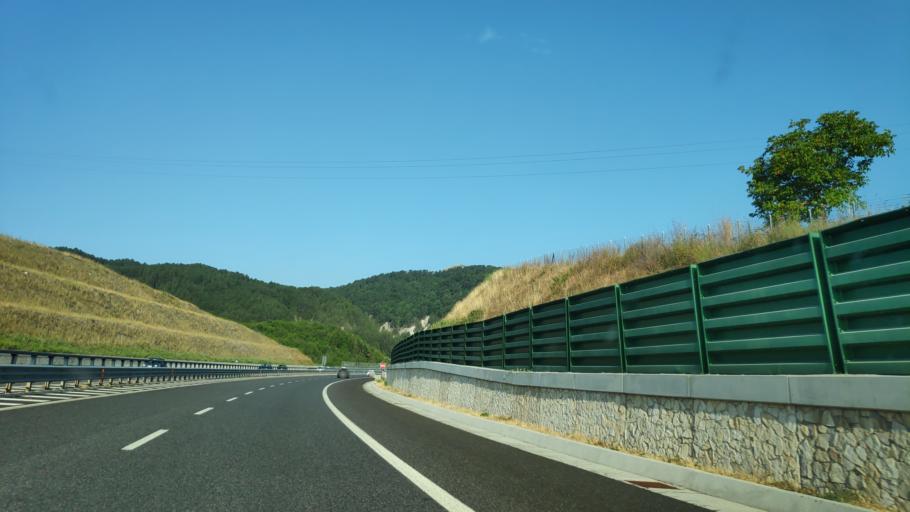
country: IT
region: Calabria
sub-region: Provincia di Cosenza
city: Mormanno
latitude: 39.8771
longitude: 15.9945
